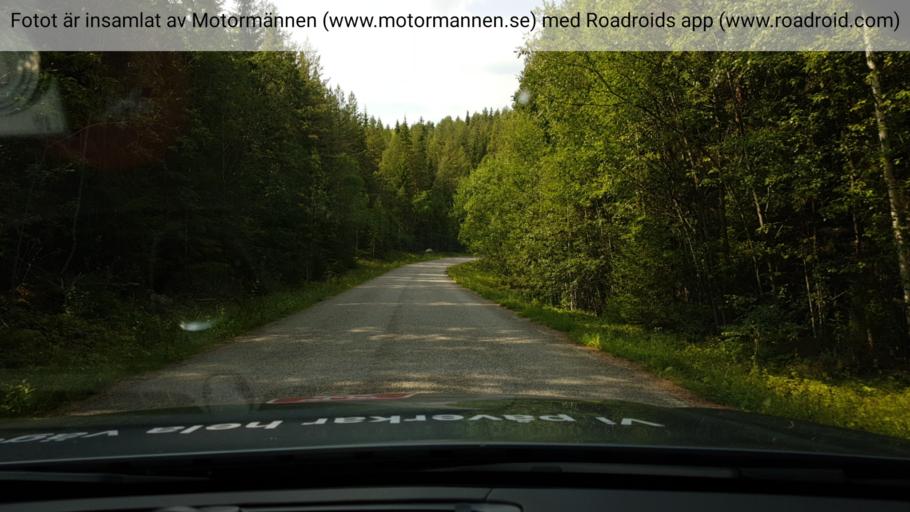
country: SE
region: Jaemtland
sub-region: OEstersunds Kommun
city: Brunflo
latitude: 62.9934
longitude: 15.0952
